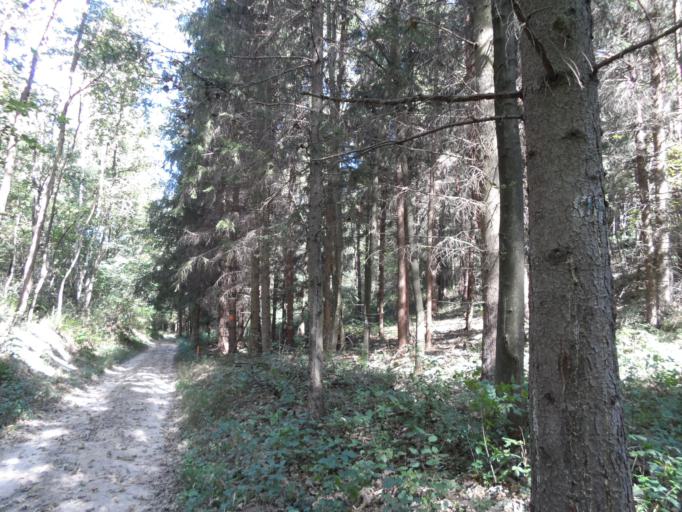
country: HU
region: Veszprem
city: Ajka
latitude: 47.2128
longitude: 17.5508
